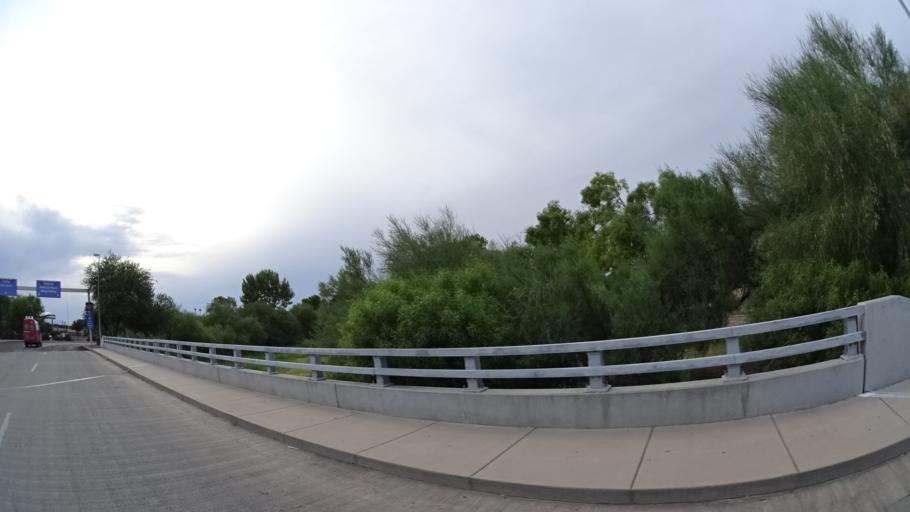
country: US
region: Arizona
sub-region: Pima County
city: Summit
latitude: 32.1228
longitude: -110.9355
